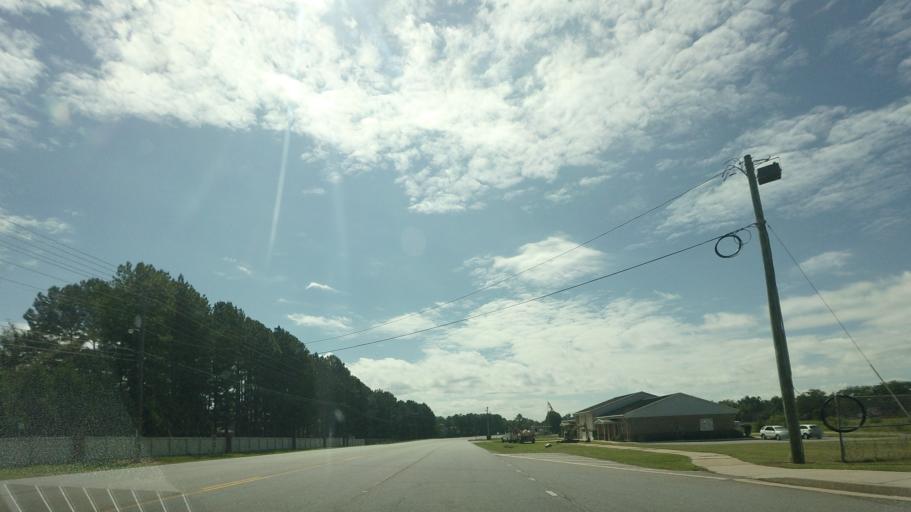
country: US
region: Georgia
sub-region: Houston County
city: Centerville
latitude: 32.5746
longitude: -83.6925
